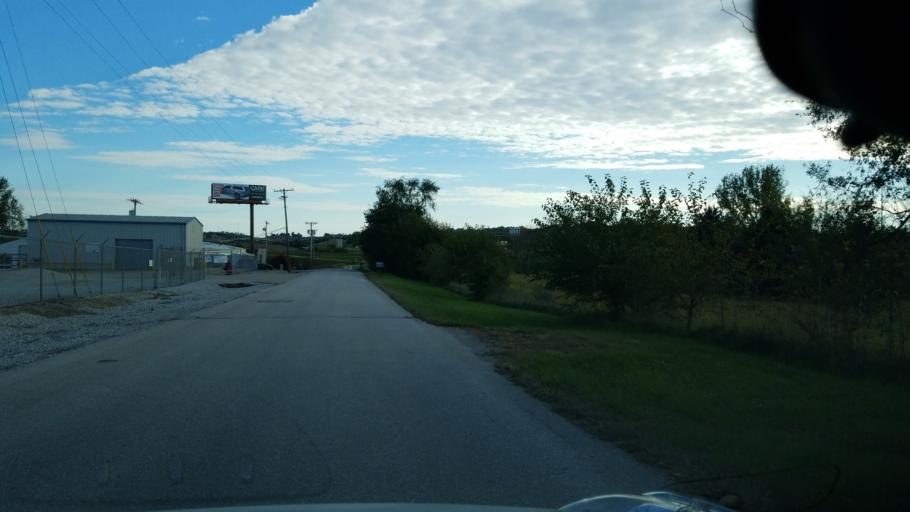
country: US
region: Nebraska
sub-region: Sarpy County
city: Offutt Air Force Base
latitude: 41.1165
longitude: -95.9328
